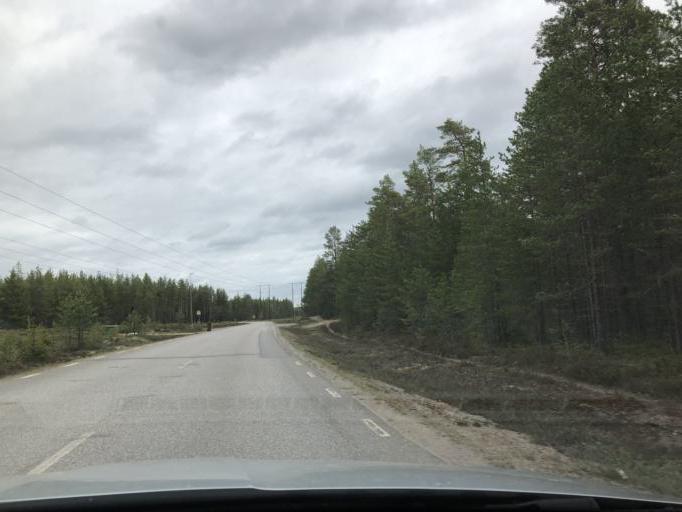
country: SE
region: Norrbotten
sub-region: Pitea Kommun
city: Pitea
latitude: 65.2386
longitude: 21.5203
